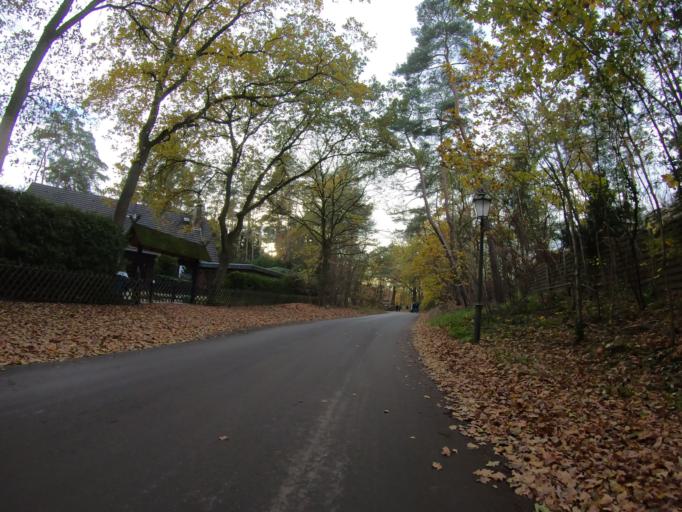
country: DE
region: Lower Saxony
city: Ribbesbuttel
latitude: 52.4619
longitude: 10.5011
